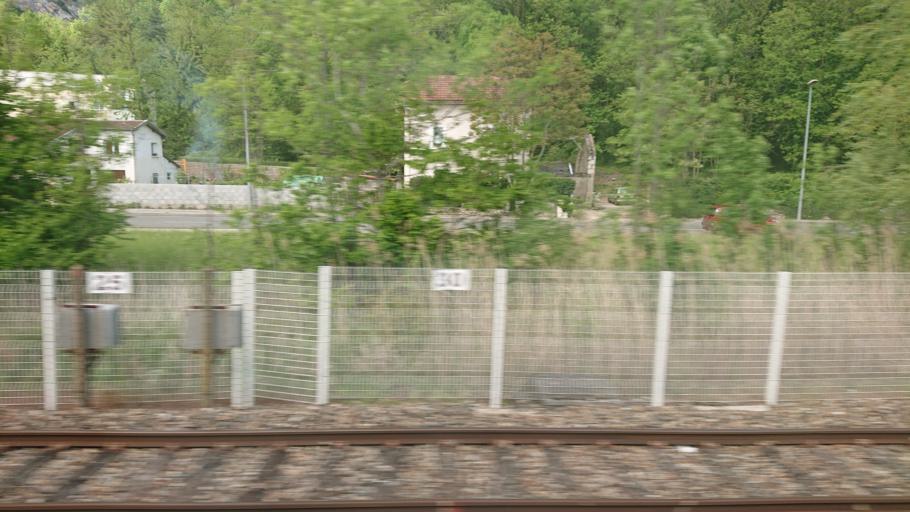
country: FR
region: Rhone-Alpes
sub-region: Departement de l'Ain
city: Culoz
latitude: 45.8438
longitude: 5.7738
